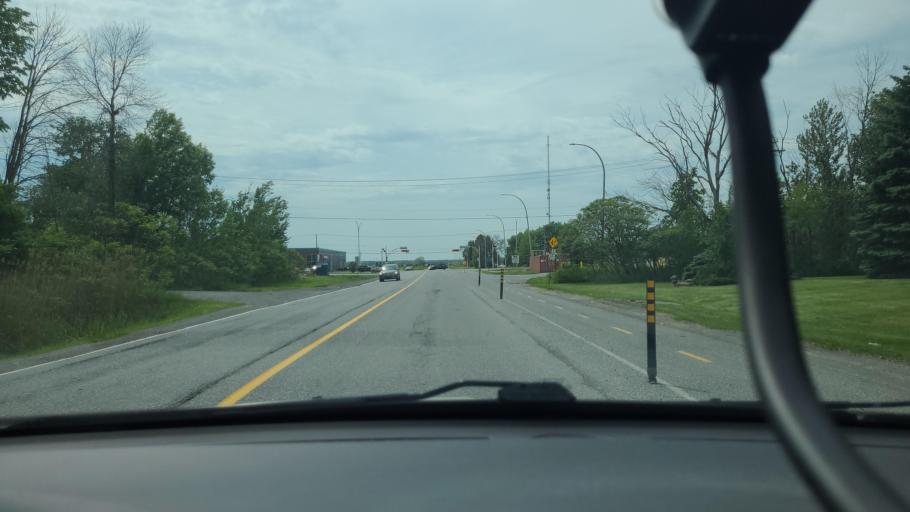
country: CA
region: Quebec
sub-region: Monteregie
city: Saint-Hyacinthe
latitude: 45.6288
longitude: -72.9949
